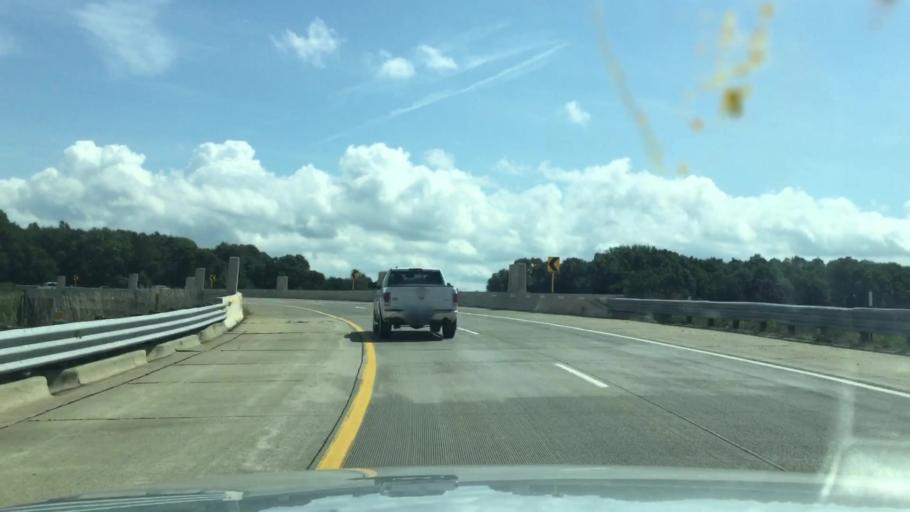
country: US
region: Michigan
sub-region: Kalamazoo County
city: Westwood
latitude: 42.2360
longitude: -85.6390
